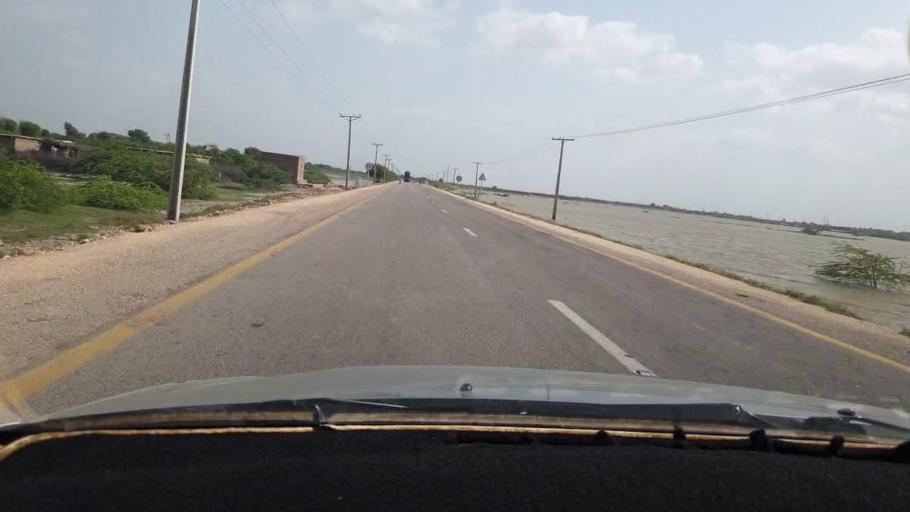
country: PK
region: Sindh
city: Naukot
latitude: 24.9287
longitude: 69.3178
